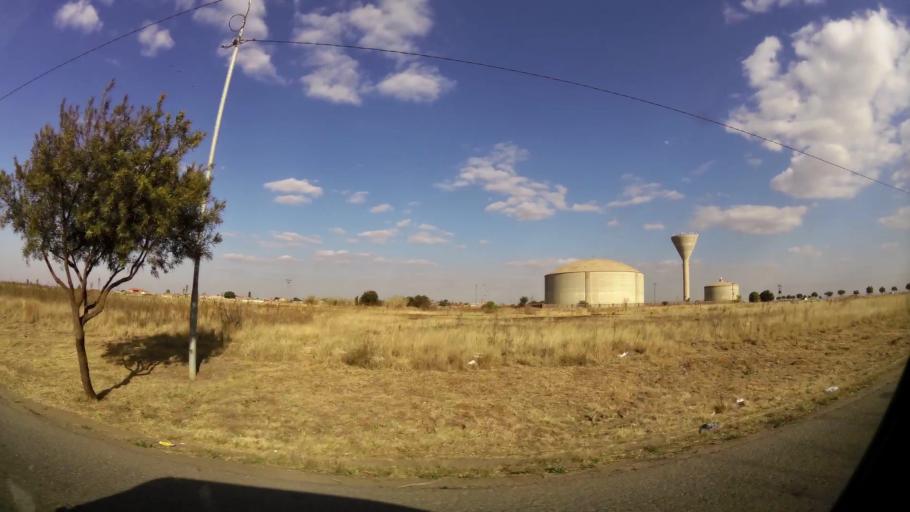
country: ZA
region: Gauteng
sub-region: City of Johannesburg Metropolitan Municipality
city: Midrand
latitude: -26.0123
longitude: 28.1642
